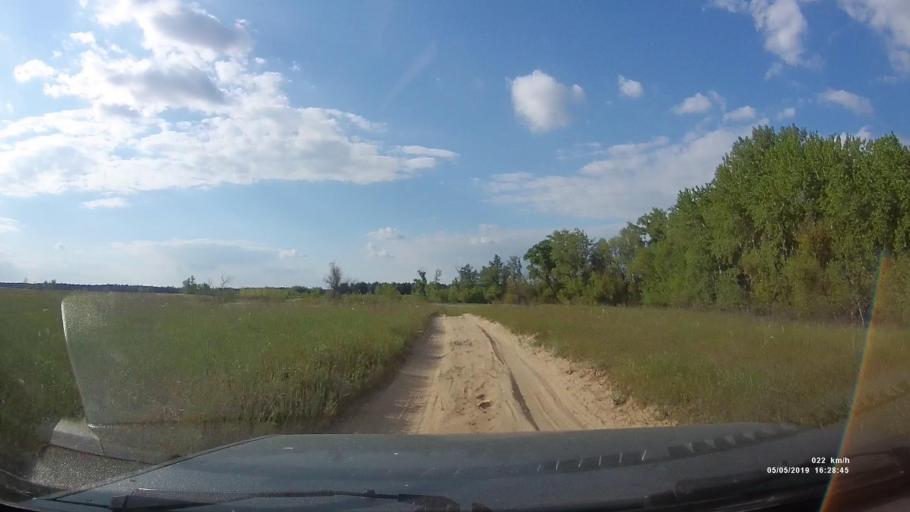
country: RU
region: Rostov
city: Ust'-Donetskiy
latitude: 47.7685
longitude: 41.0155
